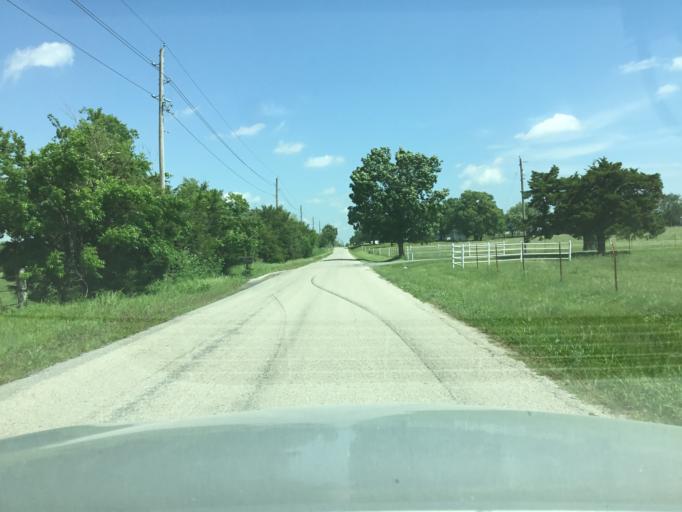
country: US
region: Kansas
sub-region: Labette County
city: Parsons
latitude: 37.3526
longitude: -95.2495
